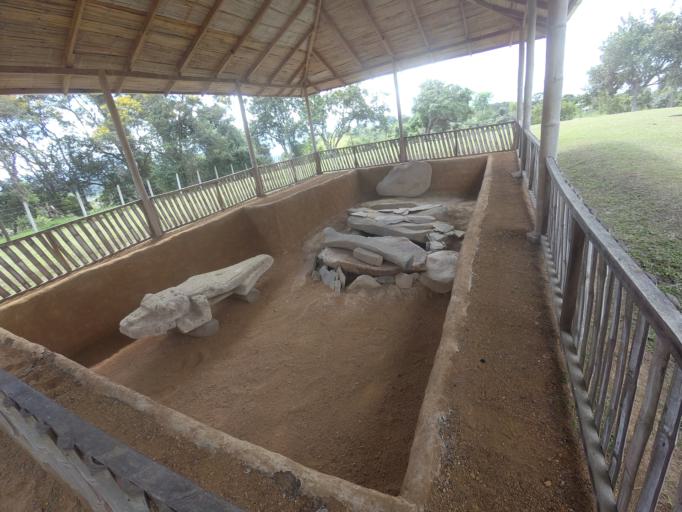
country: CO
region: Huila
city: Isnos
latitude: 1.9149
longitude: -76.2386
